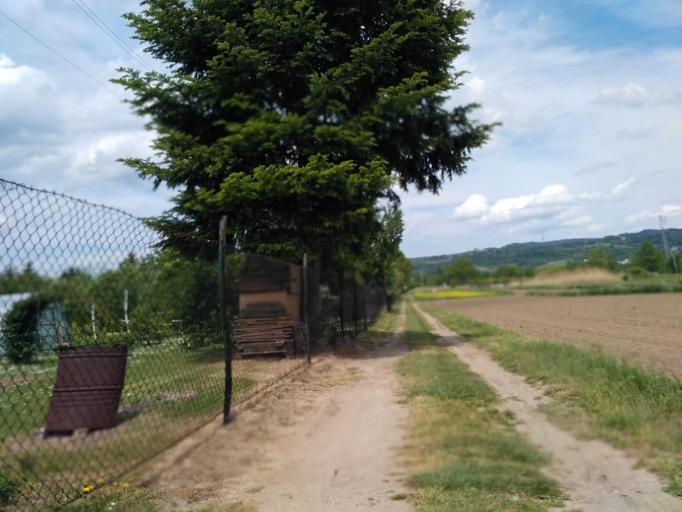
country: PL
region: Subcarpathian Voivodeship
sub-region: Powiat krosnienski
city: Odrzykon
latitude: 49.7161
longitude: 21.7552
